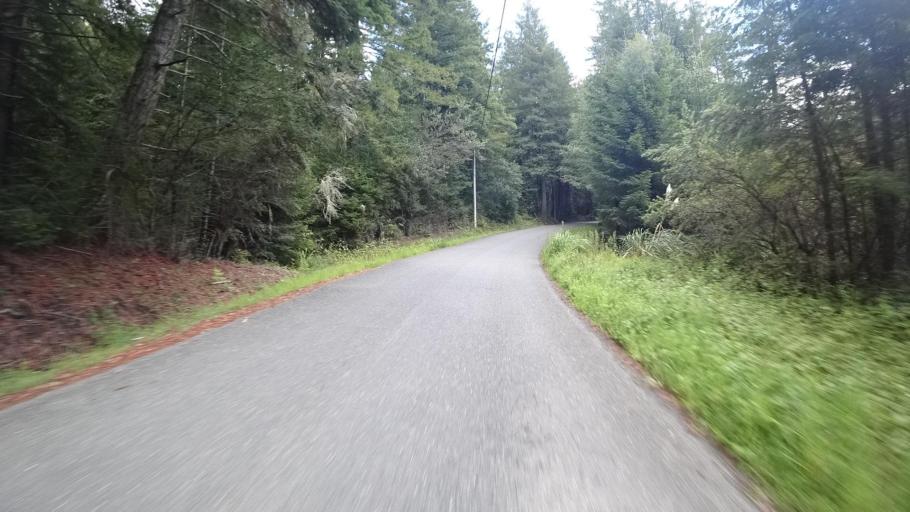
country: US
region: California
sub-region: Humboldt County
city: Blue Lake
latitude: 40.8543
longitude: -123.9297
